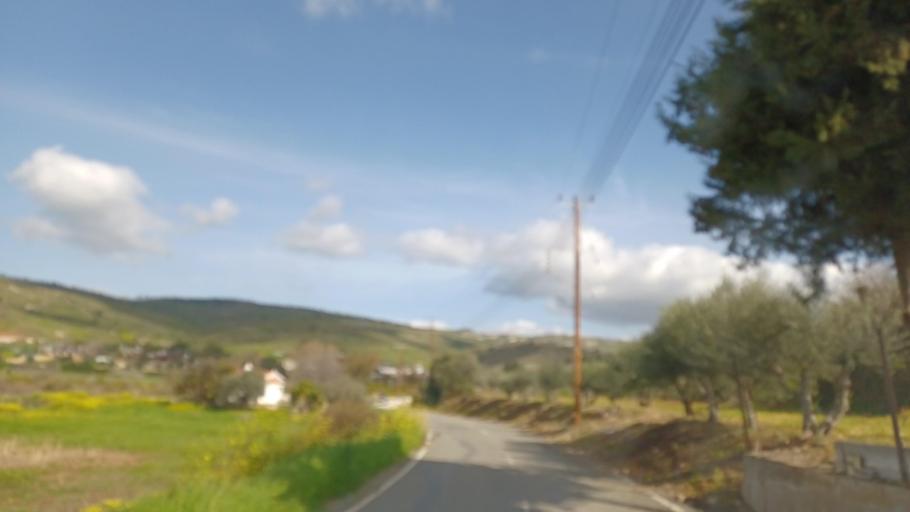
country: CY
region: Limassol
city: Pissouri
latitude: 34.7653
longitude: 32.6384
